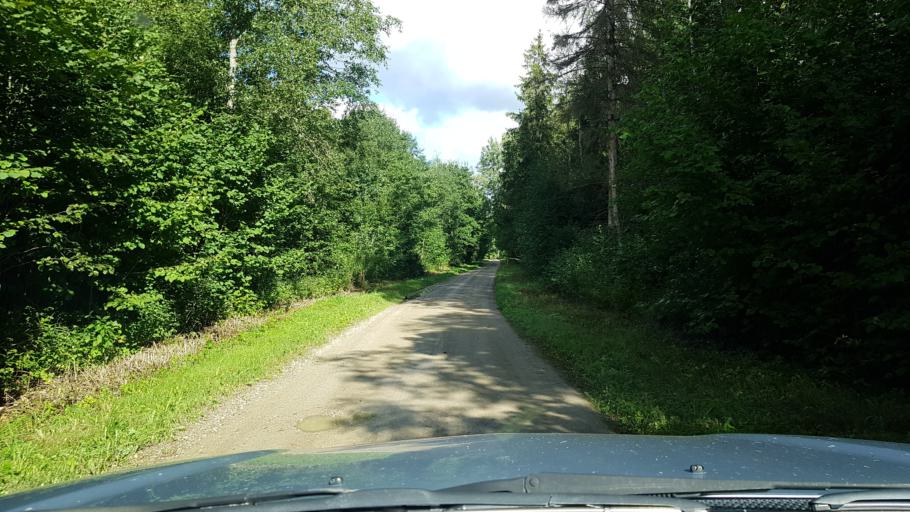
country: EE
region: Harju
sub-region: Raasiku vald
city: Arukula
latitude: 59.2588
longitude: 25.0982
